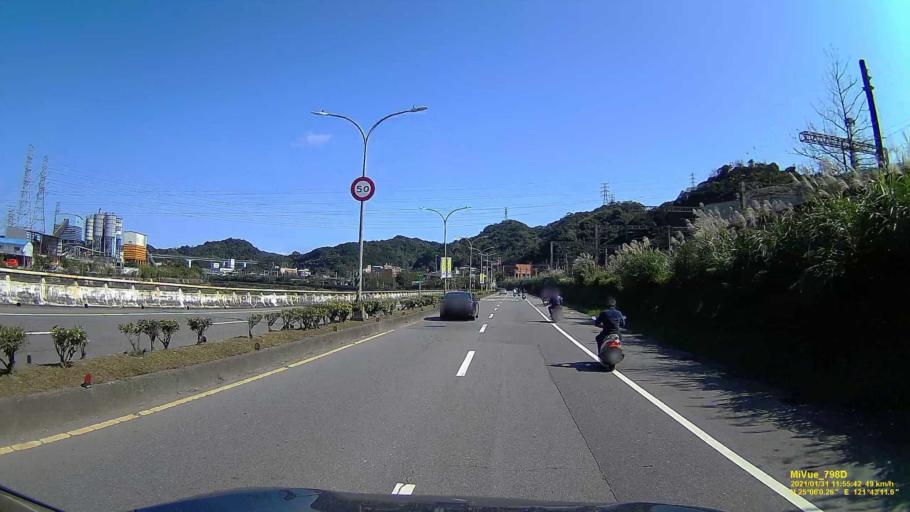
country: TW
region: Taiwan
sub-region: Keelung
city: Keelung
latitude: 25.1001
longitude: 121.7198
